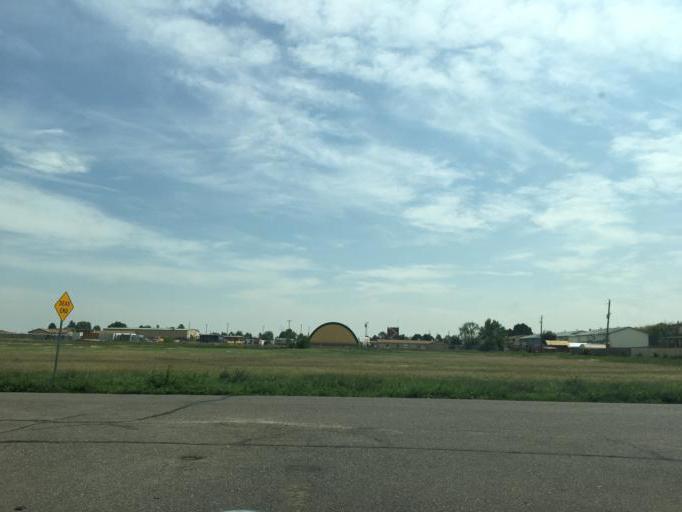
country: US
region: Colorado
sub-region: Adams County
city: Aurora
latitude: 39.7369
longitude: -104.7962
